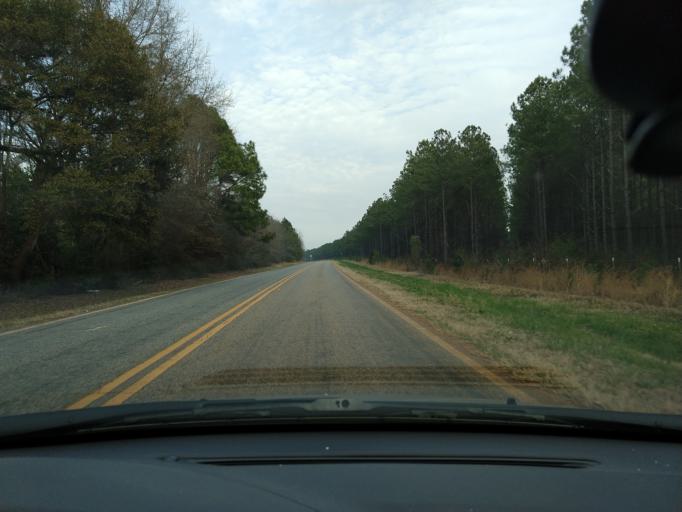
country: US
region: Georgia
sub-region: Webster County
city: Preston
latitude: 32.0213
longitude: -84.4011
